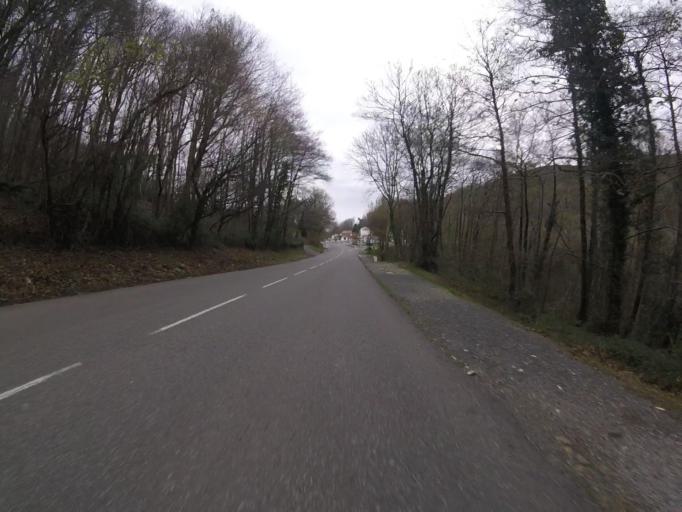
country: FR
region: Aquitaine
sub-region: Departement des Pyrenees-Atlantiques
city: Sare
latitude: 43.3268
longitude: -1.6014
